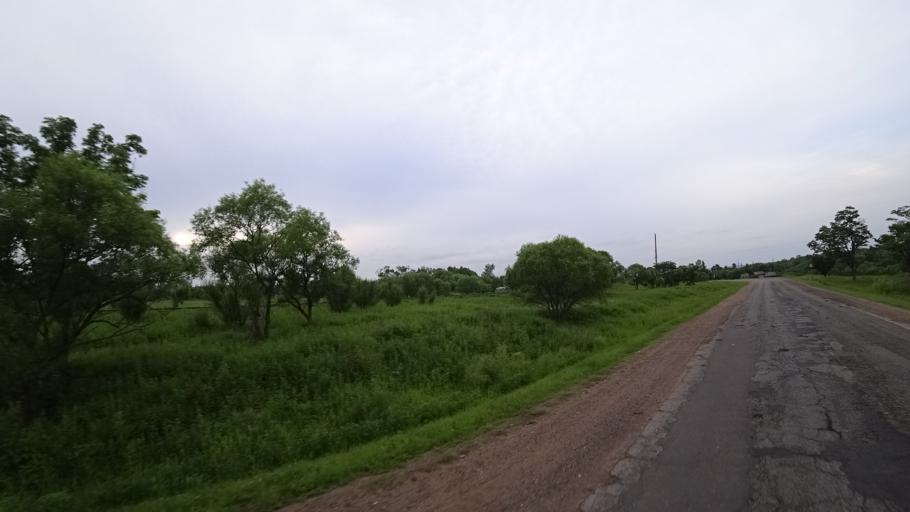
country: RU
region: Primorskiy
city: Novosysoyevka
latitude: 44.2230
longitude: 133.3501
